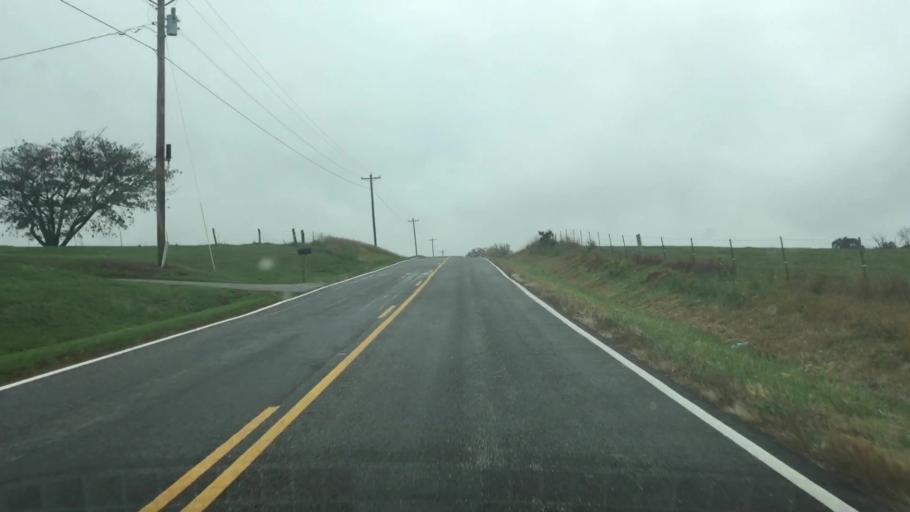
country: US
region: Missouri
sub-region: Callaway County
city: Fulton
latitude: 38.8294
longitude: -91.9158
